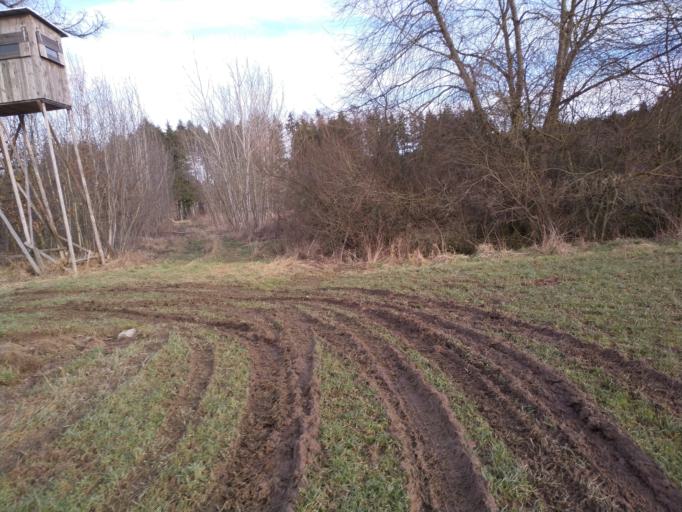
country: DE
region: Bavaria
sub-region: Swabia
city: Rettenbach
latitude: 48.4263
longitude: 10.3218
